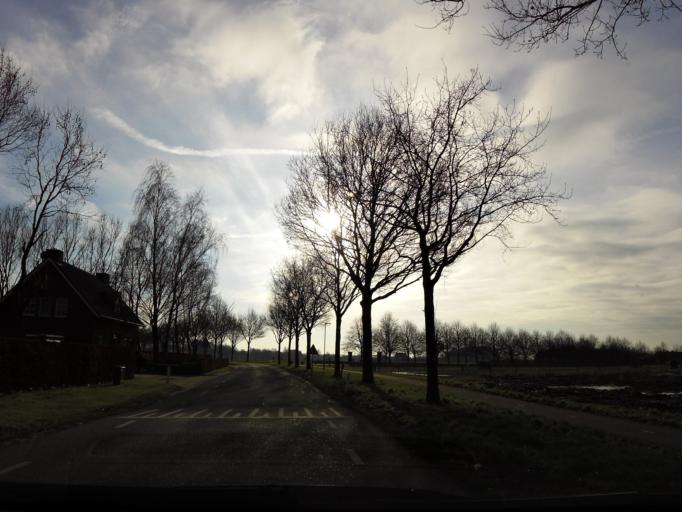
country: NL
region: Limburg
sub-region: Gemeente Beesel
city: Beesel
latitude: 51.2498
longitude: 6.0301
